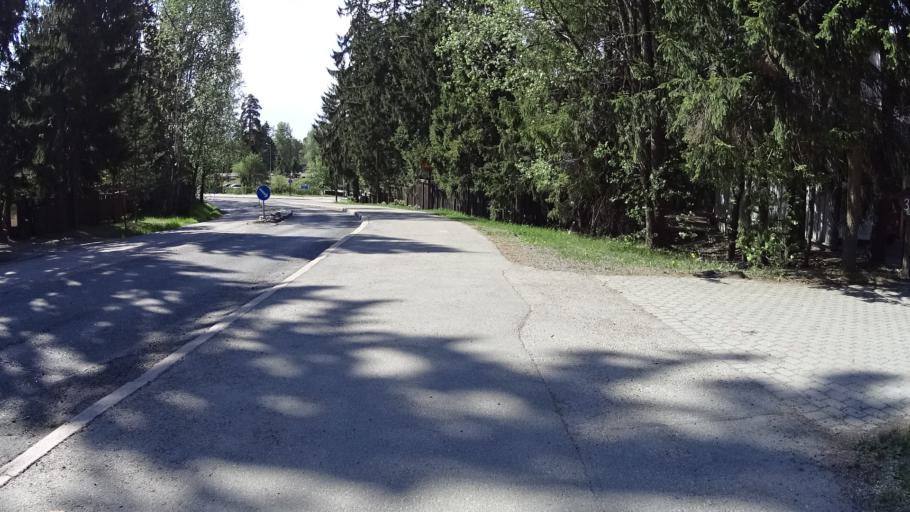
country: FI
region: Uusimaa
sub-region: Helsinki
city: Kauniainen
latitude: 60.2178
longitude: 24.7101
